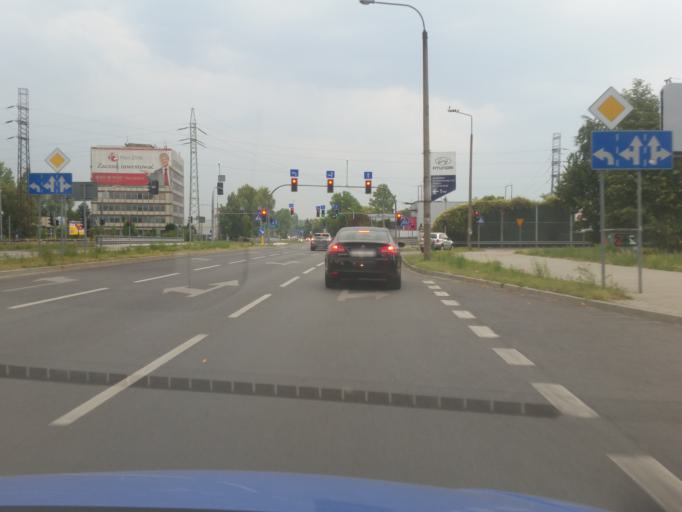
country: PL
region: Silesian Voivodeship
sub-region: Sosnowiec
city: Sosnowiec
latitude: 50.2891
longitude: 19.1119
